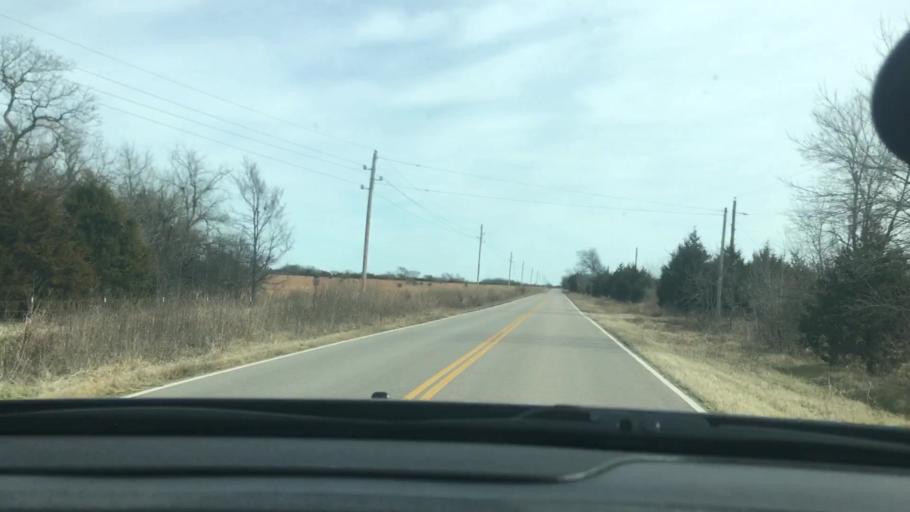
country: US
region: Oklahoma
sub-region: Murray County
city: Sulphur
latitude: 34.4048
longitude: -96.8575
